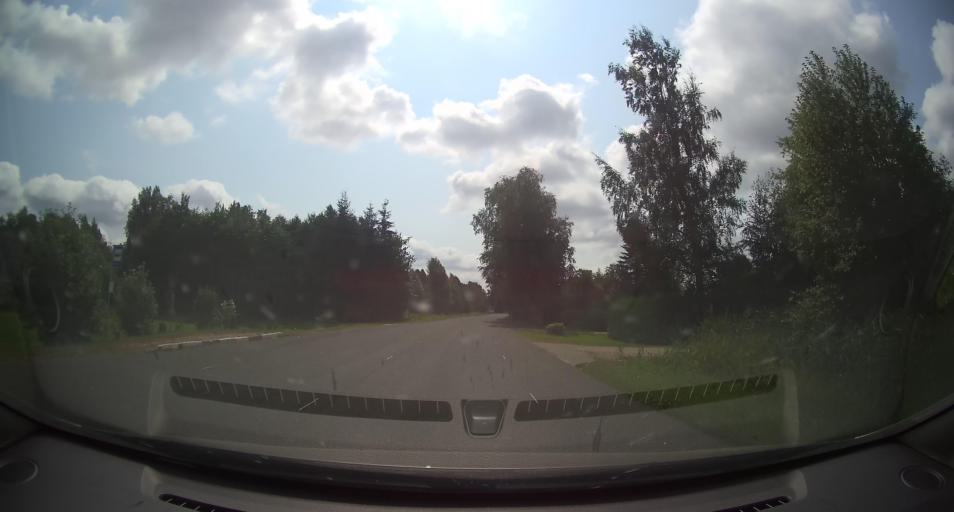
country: EE
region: Paernumaa
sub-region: Audru vald
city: Audru
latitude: 58.4950
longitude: 24.3360
